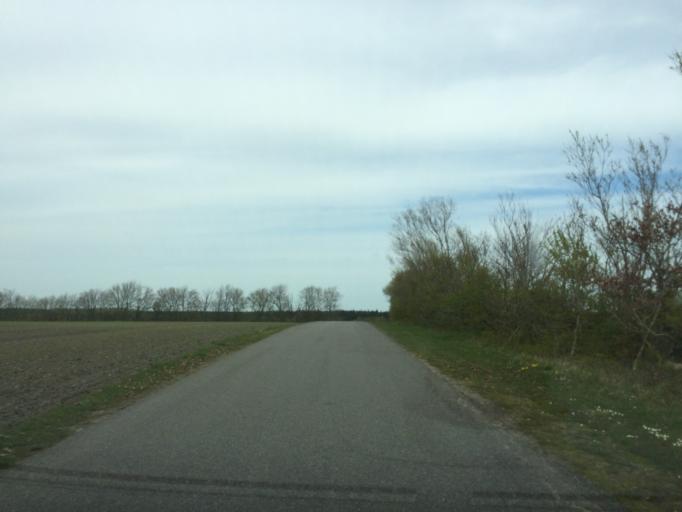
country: DK
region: Central Jutland
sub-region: Ringkobing-Skjern Kommune
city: Videbaek
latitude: 56.2039
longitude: 8.5072
